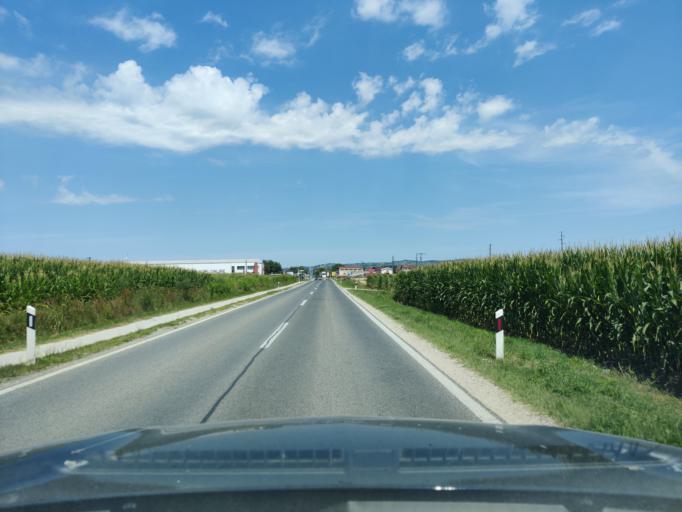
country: HR
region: Medimurska
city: Vratisinec
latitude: 46.5005
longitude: 16.4300
